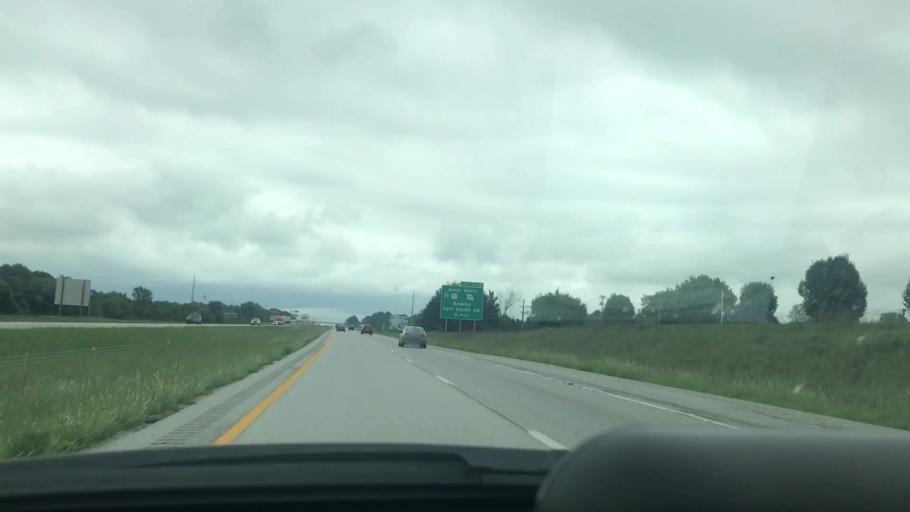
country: US
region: Missouri
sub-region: Jasper County
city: Duquesne
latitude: 37.0478
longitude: -94.4670
